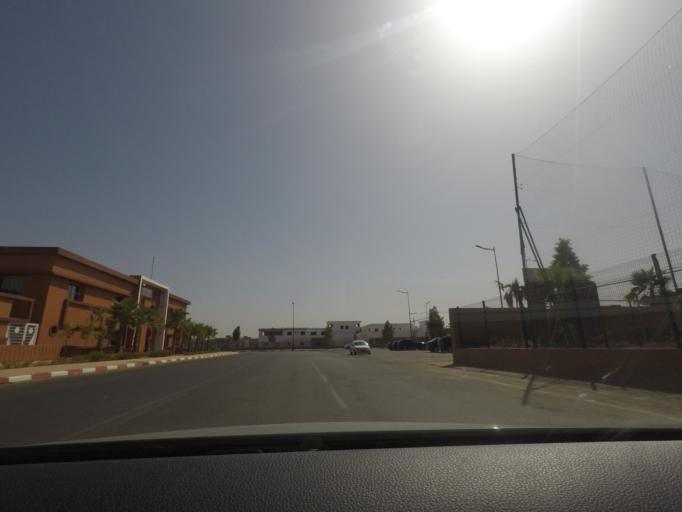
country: MA
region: Marrakech-Tensift-Al Haouz
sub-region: Marrakech
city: Marrakesh
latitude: 31.5891
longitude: -8.0299
